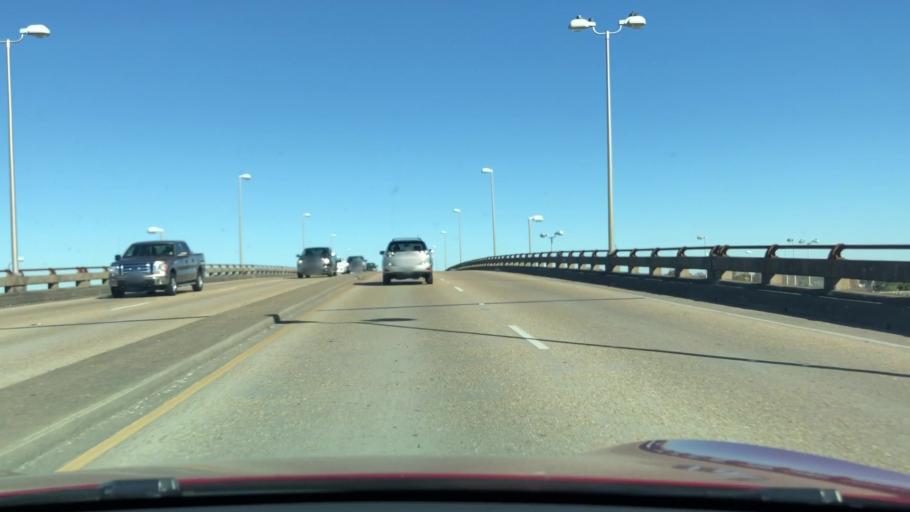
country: US
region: Louisiana
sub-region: Jefferson Parish
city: Jefferson
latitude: 29.9736
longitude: -90.1564
